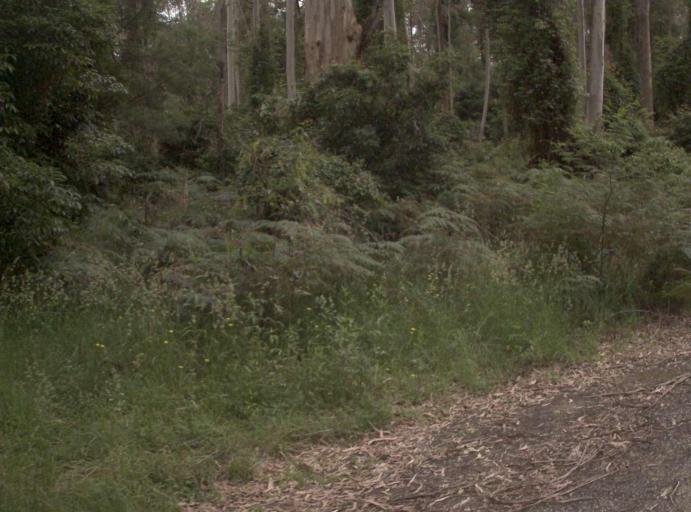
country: AU
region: New South Wales
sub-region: Bombala
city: Bombala
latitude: -37.4624
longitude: 149.1866
